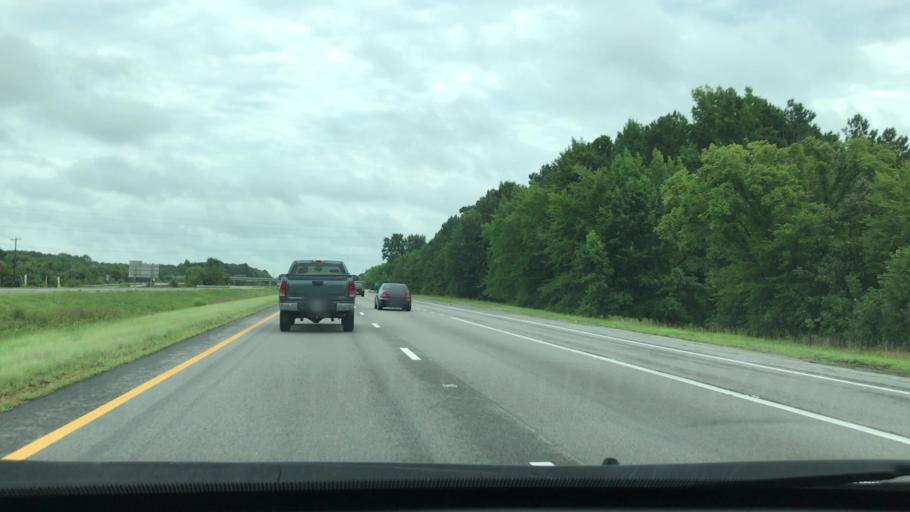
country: US
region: Virginia
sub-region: Sussex County
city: Sussex
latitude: 36.9469
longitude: -77.3921
